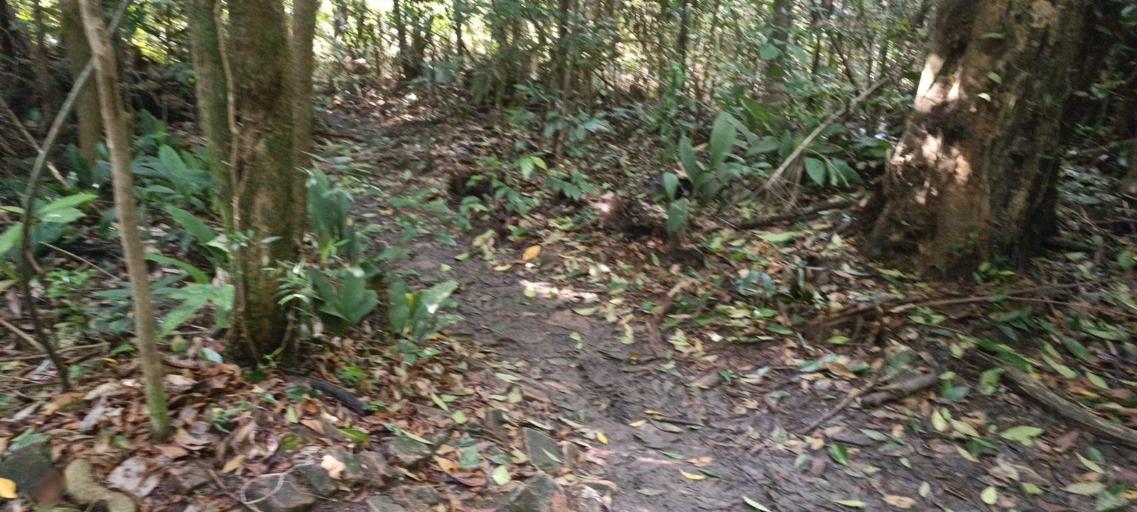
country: MY
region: Penang
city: Tanjung Tokong
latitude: 5.4438
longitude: 100.2930
